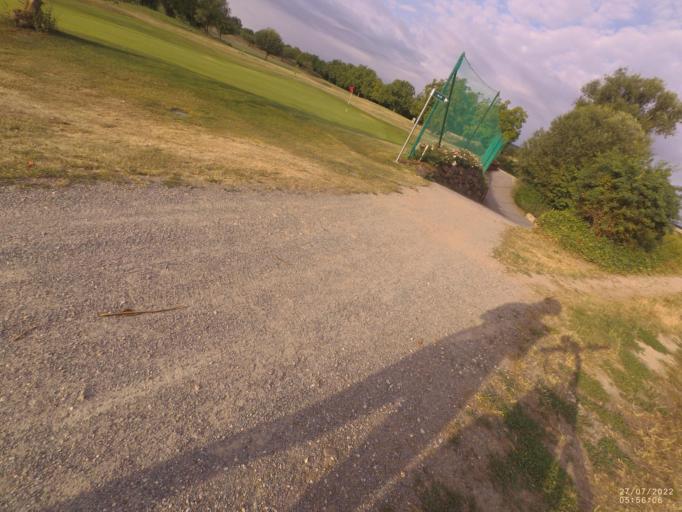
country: DE
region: Rheinland-Pfalz
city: Dackenheim
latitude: 49.5271
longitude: 8.1787
